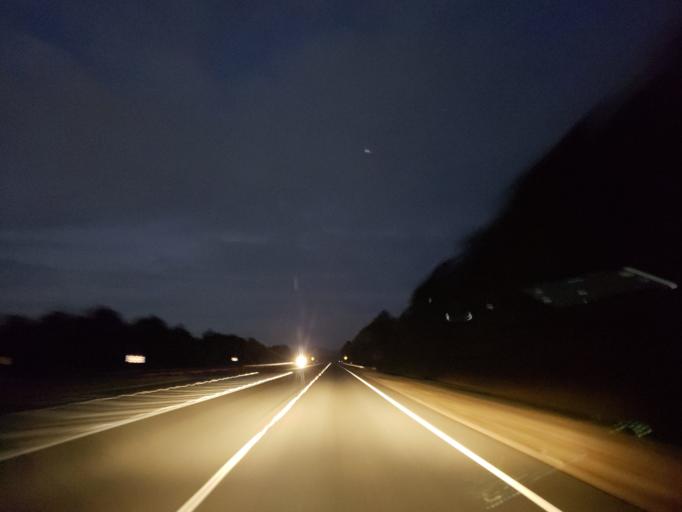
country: US
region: Georgia
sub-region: Polk County
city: Rockmart
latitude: 33.9957
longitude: -85.0257
